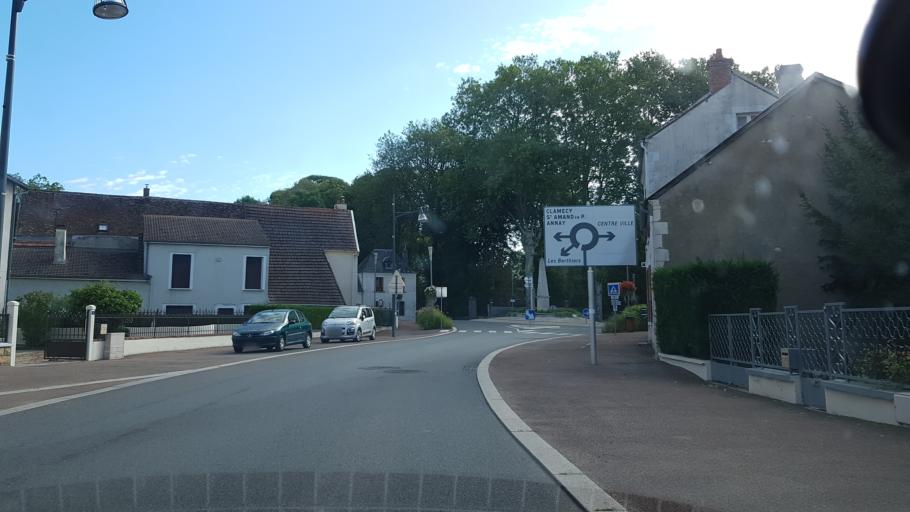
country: FR
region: Bourgogne
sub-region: Departement de la Nievre
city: Neuvy-sur-Loire
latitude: 47.5248
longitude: 2.8799
